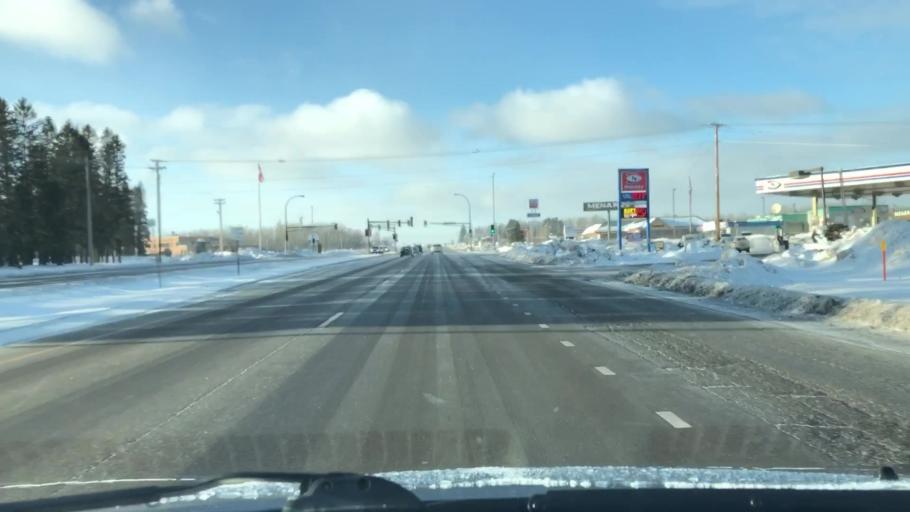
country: US
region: Minnesota
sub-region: Saint Louis County
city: Hermantown
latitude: 46.8212
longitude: -92.1850
